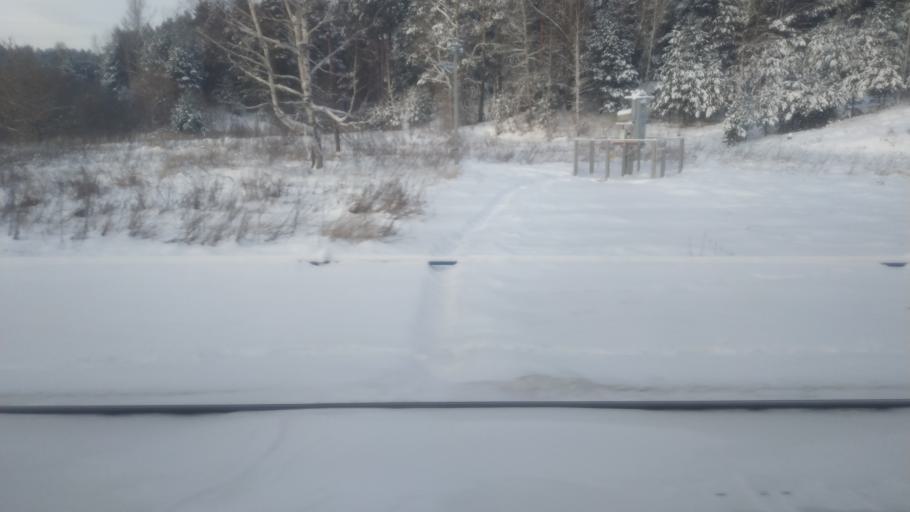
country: RU
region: Kirov
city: Krasnaya Polyana
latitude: 56.2474
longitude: 51.1956
